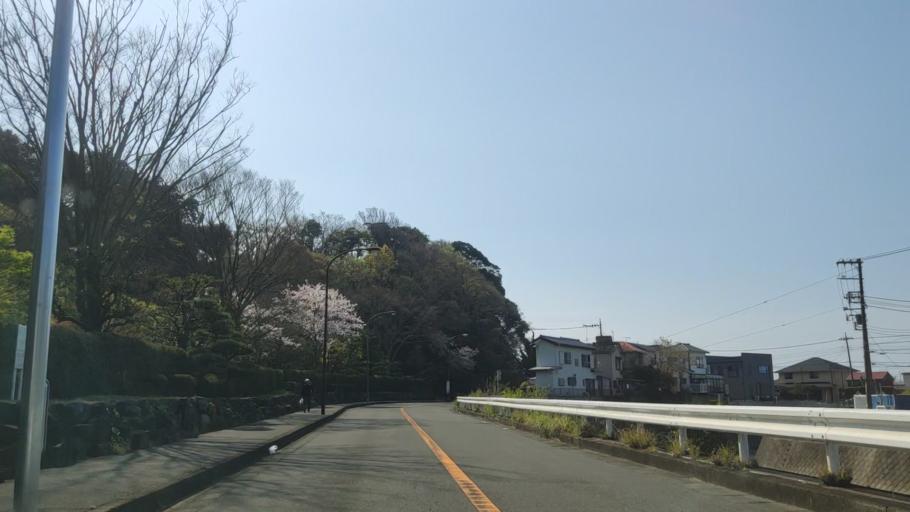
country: JP
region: Kanagawa
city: Oiso
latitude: 35.3065
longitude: 139.2888
